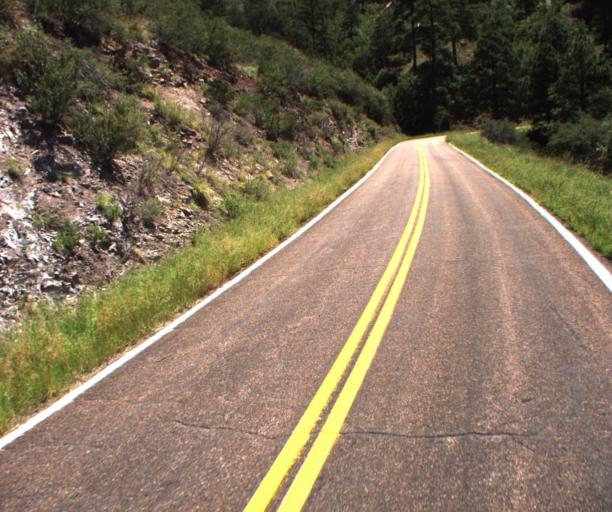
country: US
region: Arizona
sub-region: Greenlee County
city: Morenci
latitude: 33.2239
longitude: -109.3886
